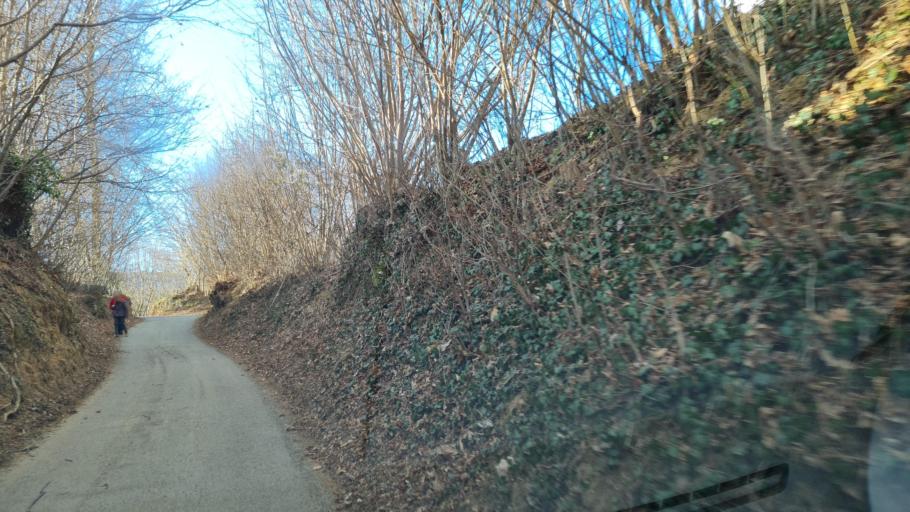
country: IT
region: Piedmont
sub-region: Provincia di Biella
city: Muzzano
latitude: 45.5740
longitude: 7.9913
